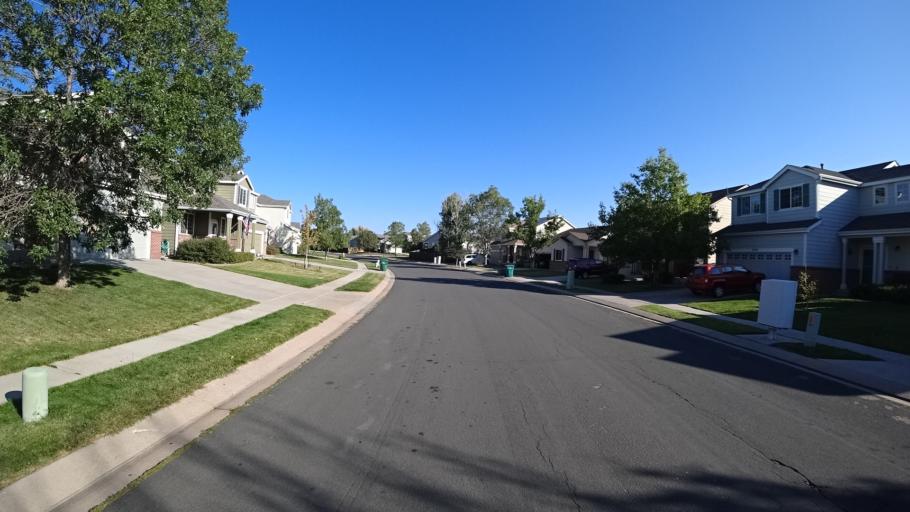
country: US
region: Colorado
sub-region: El Paso County
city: Cimarron Hills
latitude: 38.8845
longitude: -104.6920
